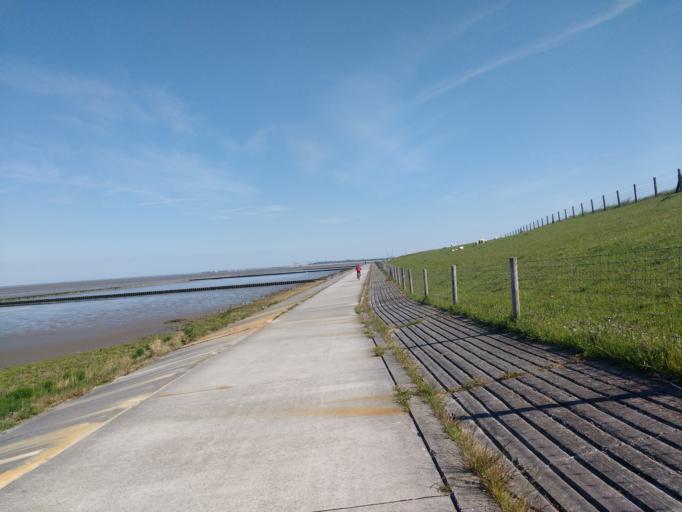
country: DE
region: Lower Saxony
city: Schillig
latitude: 53.6821
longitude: 8.0217
